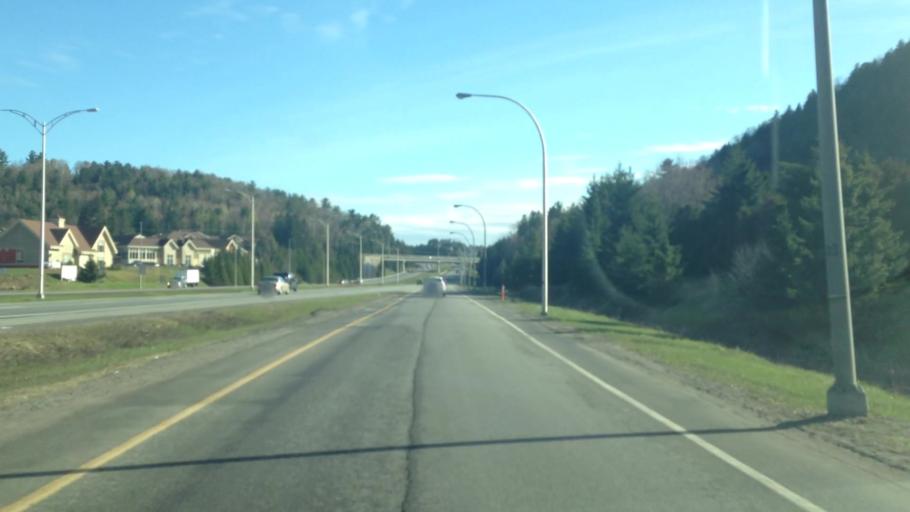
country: CA
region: Quebec
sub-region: Laurentides
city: Saint-Sauveur
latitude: 45.8953
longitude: -74.1464
